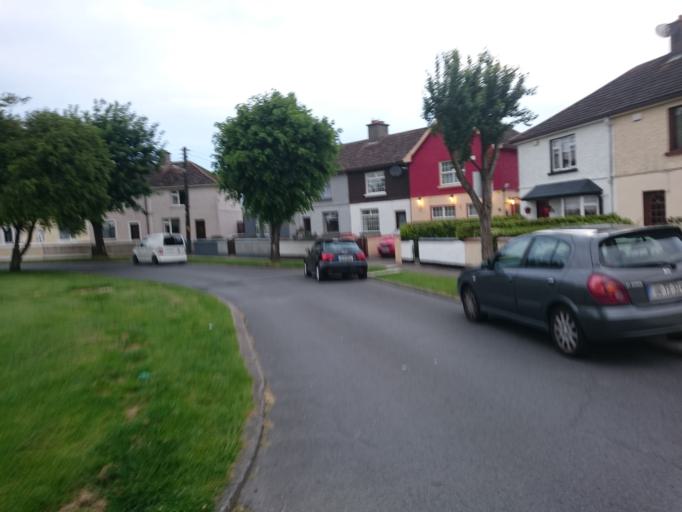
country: IE
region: Leinster
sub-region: Kilkenny
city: Kilkenny
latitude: 52.6519
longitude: -7.2637
